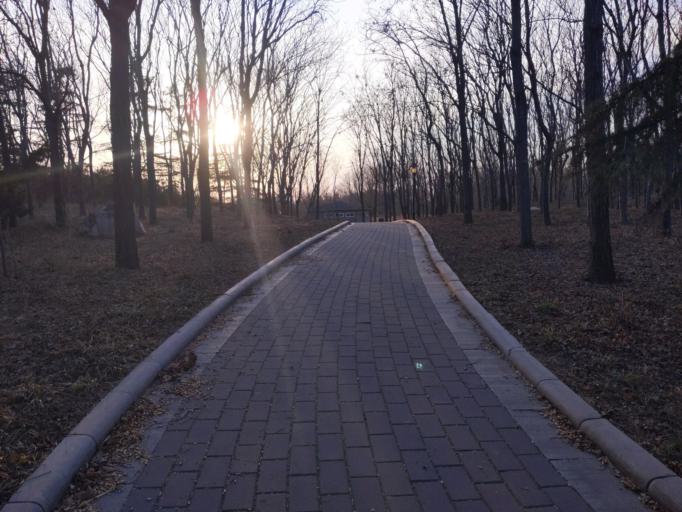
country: CN
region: Henan Sheng
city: Puyang
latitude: 35.7841
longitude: 114.9507
